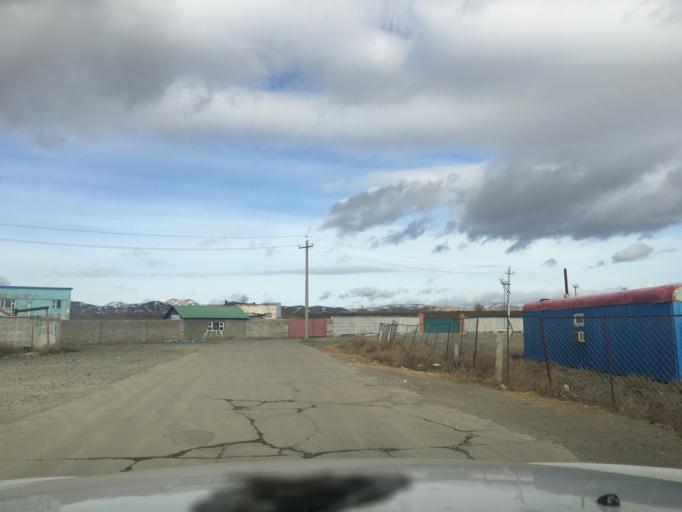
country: MN
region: Ulaanbaatar
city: Ulaanbaatar
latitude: 47.9025
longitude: 106.7384
